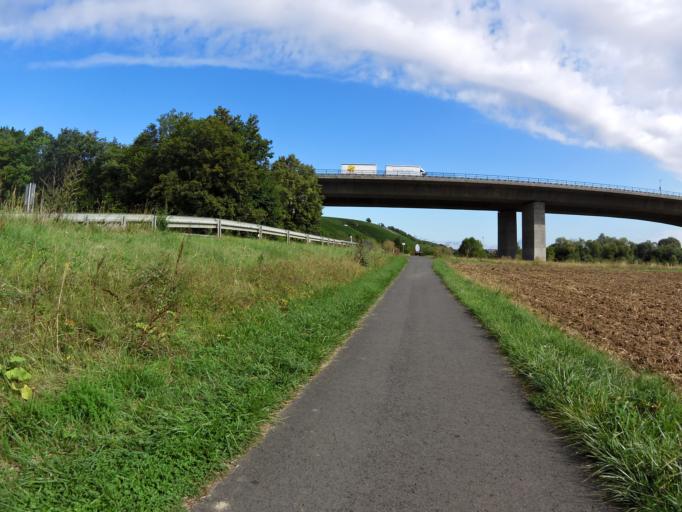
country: DE
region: Bavaria
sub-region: Regierungsbezirk Unterfranken
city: Mainstockheim
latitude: 49.7845
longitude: 10.1514
